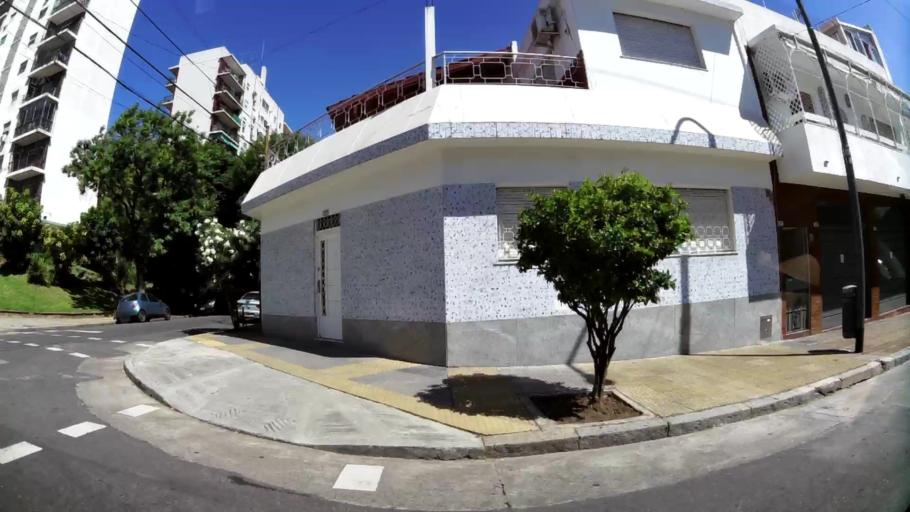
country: AR
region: Buenos Aires F.D.
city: Villa Santa Rita
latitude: -34.6338
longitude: -58.4509
